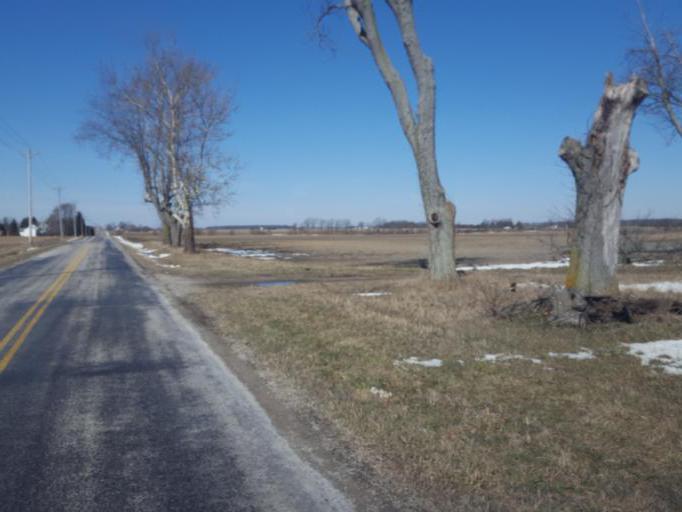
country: US
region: Ohio
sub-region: Marion County
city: Marion
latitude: 40.6587
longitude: -83.1984
